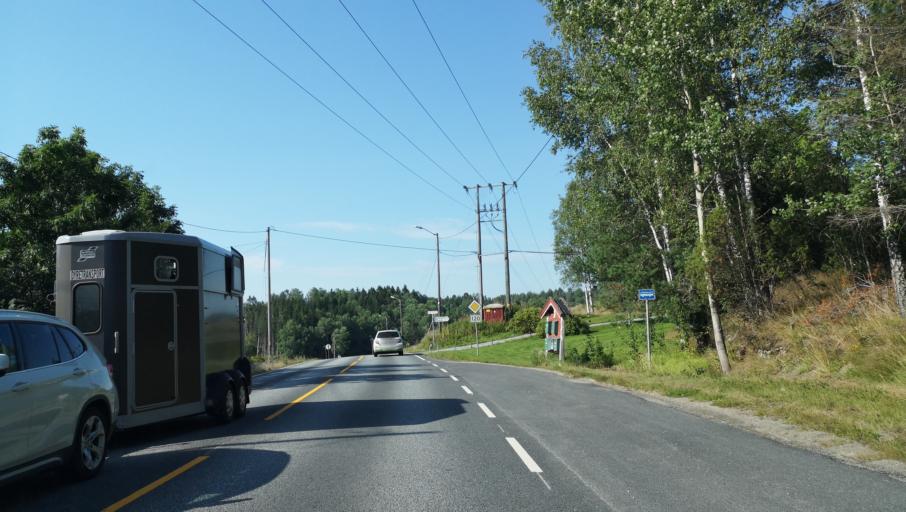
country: NO
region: Ostfold
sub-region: Valer
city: Kirkebygda
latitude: 59.5461
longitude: 10.8485
